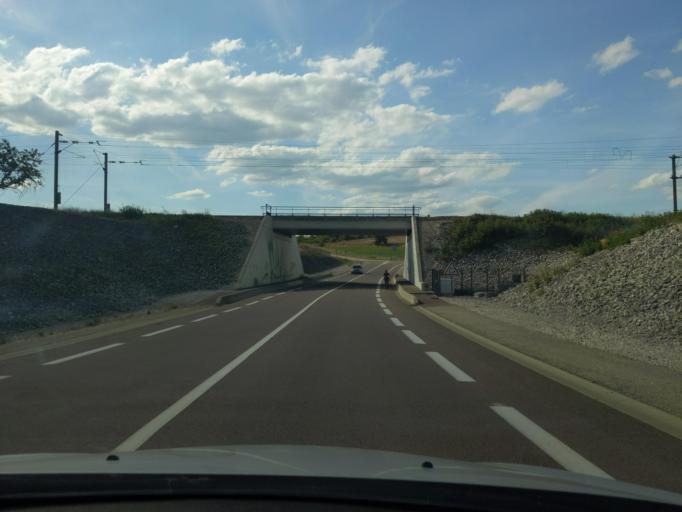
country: FR
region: Bourgogne
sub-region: Departement de la Cote-d'Or
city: Ruffey-les-Echirey
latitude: 47.3657
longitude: 5.0726
